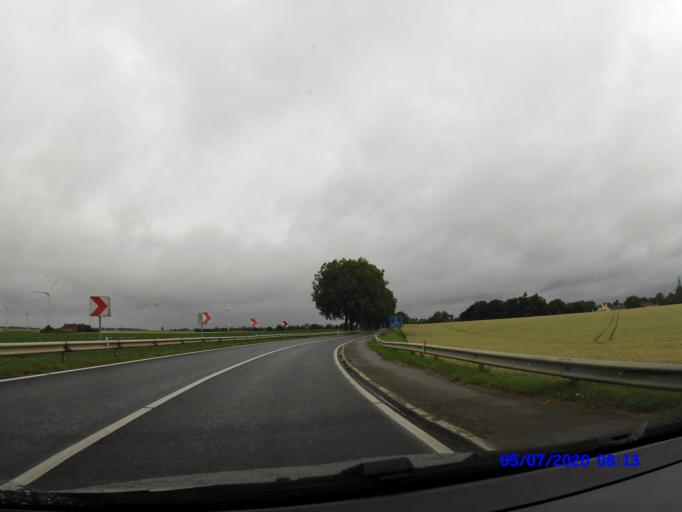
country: BE
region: Wallonia
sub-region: Province du Brabant Wallon
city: Villers-la-Ville
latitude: 50.5387
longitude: 4.5375
